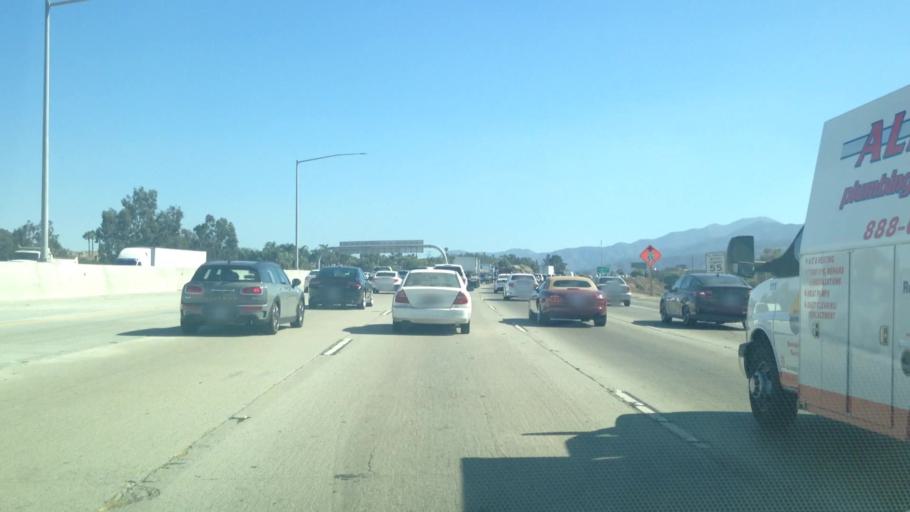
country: US
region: California
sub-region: Riverside County
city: El Cerrito
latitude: 33.8577
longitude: -117.5384
